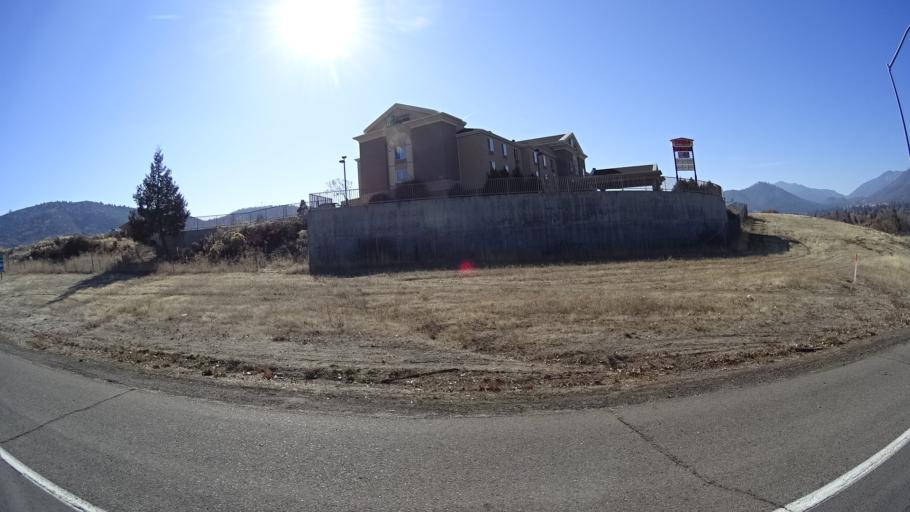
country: US
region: California
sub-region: Siskiyou County
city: Yreka
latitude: 41.7389
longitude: -122.6261
